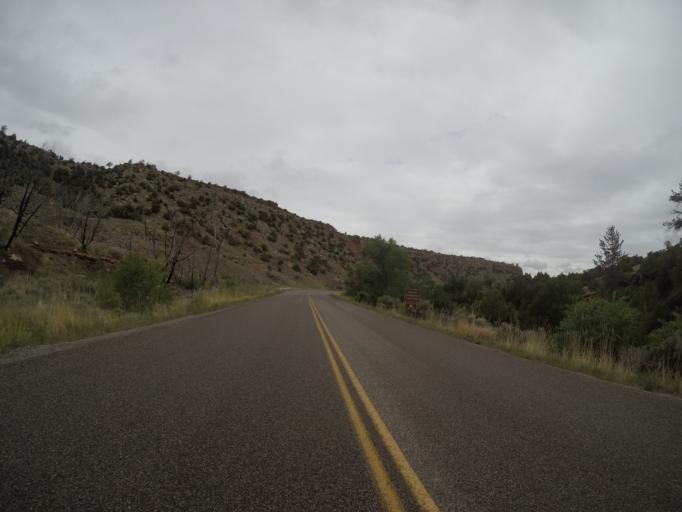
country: US
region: Wyoming
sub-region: Big Horn County
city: Lovell
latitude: 45.1074
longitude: -108.2296
